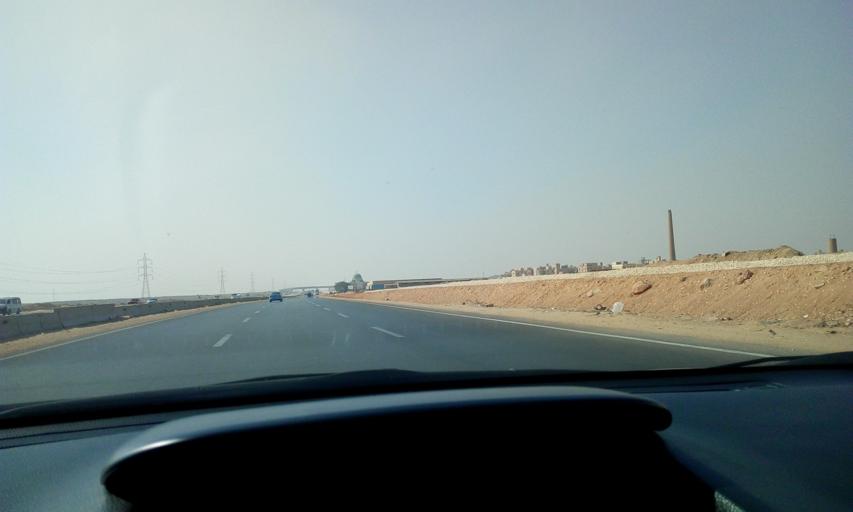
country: EG
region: Al Jizah
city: Madinat Sittah Uktubar
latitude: 29.9237
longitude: 31.0950
